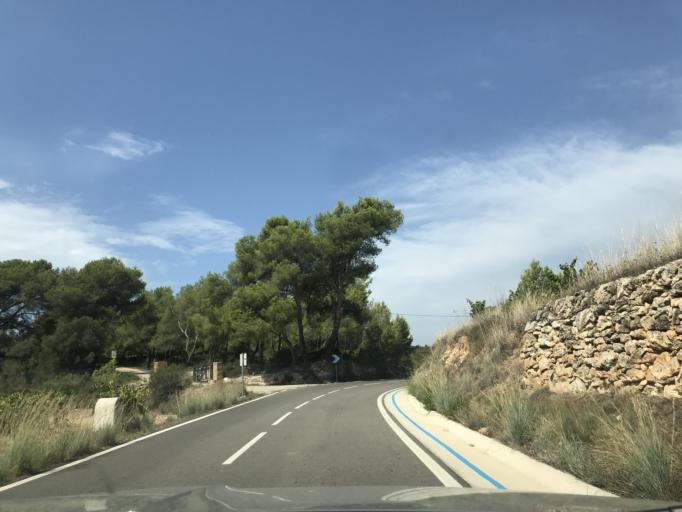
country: ES
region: Catalonia
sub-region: Provincia de Tarragona
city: Salomo
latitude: 41.2118
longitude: 1.3845
